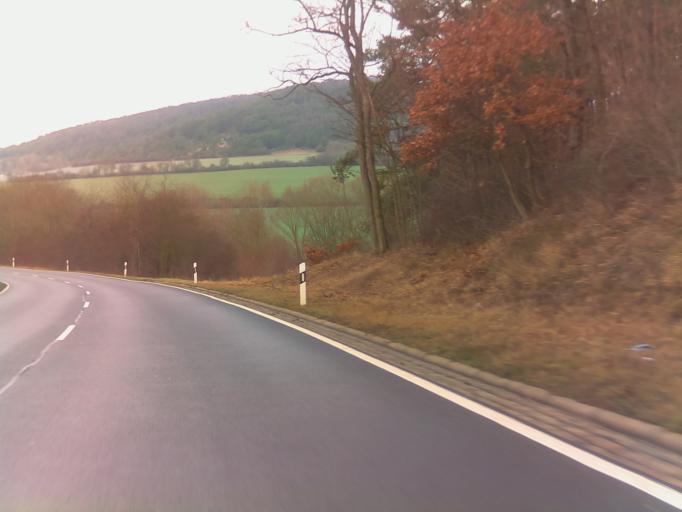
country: DE
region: Bavaria
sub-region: Regierungsbezirk Unterfranken
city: Nudlingen
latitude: 50.2254
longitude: 10.1444
